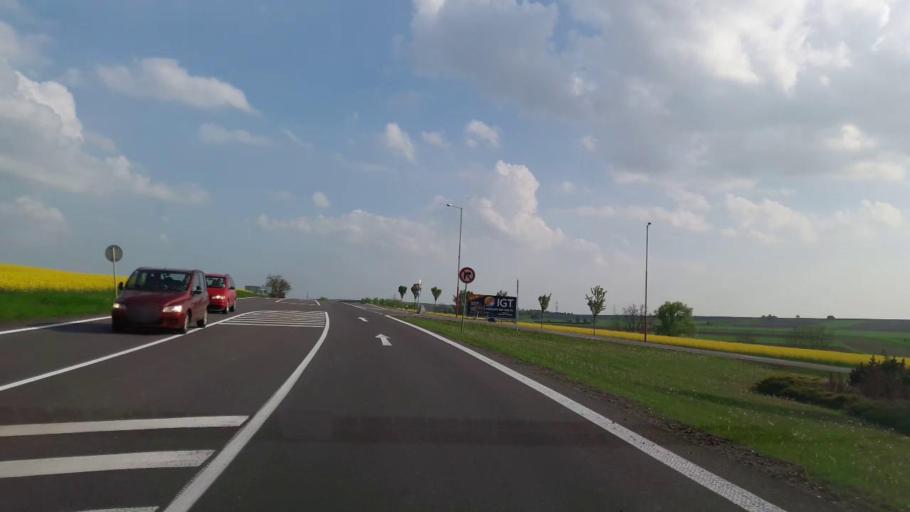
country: CZ
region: South Moravian
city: Vrbovec
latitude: 48.7602
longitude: 16.0634
